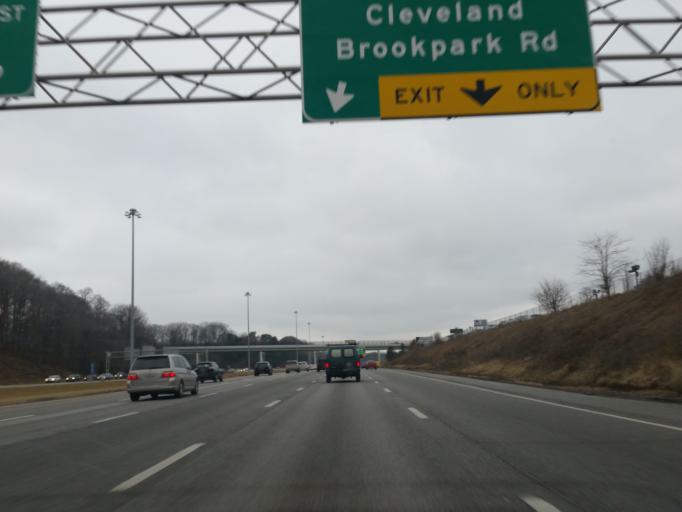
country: US
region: Ohio
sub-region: Cuyahoga County
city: Seven Hills
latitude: 41.4101
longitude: -81.6617
